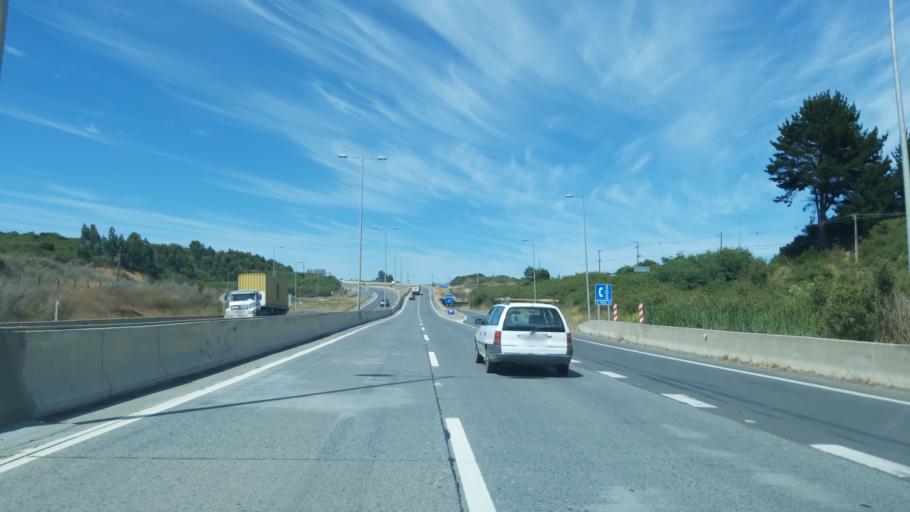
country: CL
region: Biobio
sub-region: Provincia de Concepcion
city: Coronel
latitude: -37.0438
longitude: -73.1396
